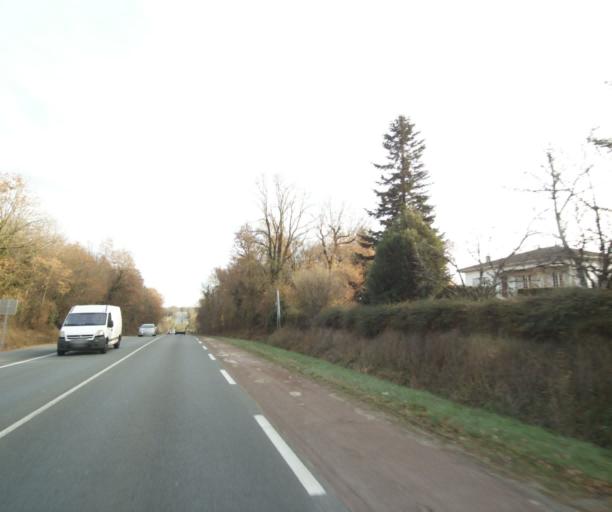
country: FR
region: Poitou-Charentes
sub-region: Departement de la Charente-Maritime
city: Saintes
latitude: 45.7612
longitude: -0.6686
